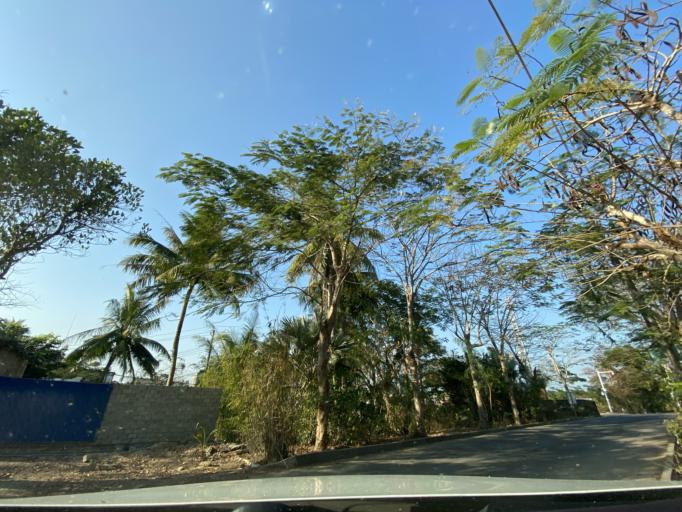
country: CN
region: Hainan
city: Yingzhou
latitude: 18.3867
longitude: 109.8205
